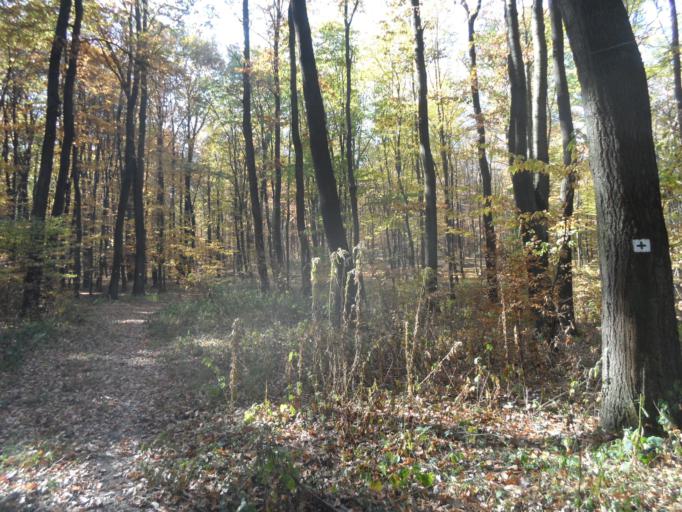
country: HU
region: Veszprem
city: Ajka
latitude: 47.1961
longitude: 17.5676
